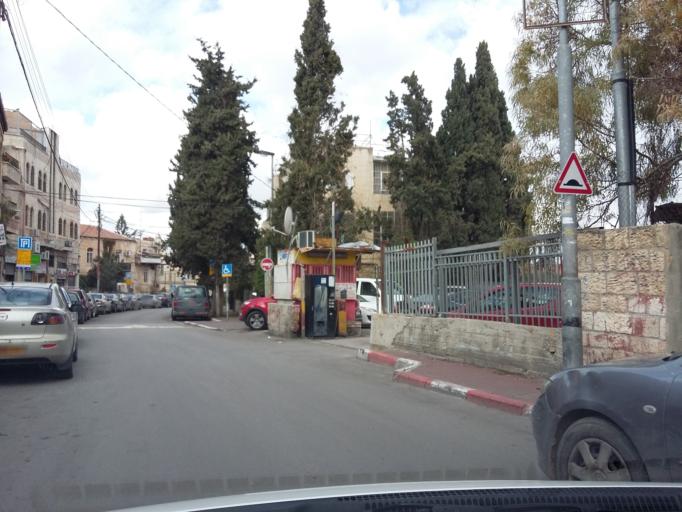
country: PS
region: West Bank
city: East Jerusalem
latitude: 31.7862
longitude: 35.2346
